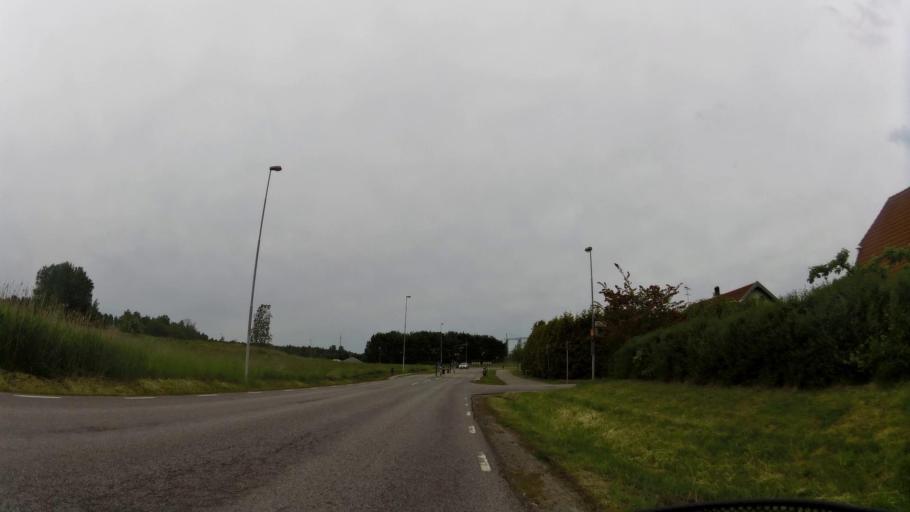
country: SE
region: OEstergoetland
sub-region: Linkopings Kommun
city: Malmslatt
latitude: 58.3894
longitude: 15.5547
